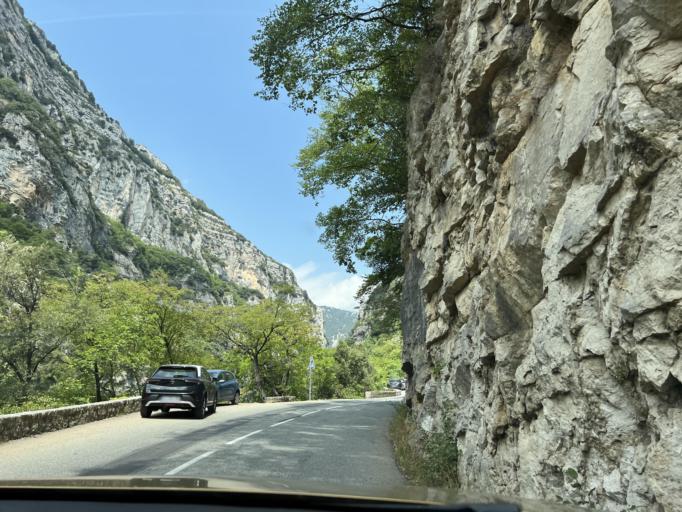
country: FR
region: Provence-Alpes-Cote d'Azur
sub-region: Departement des Alpes-Maritimes
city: Tourrettes-sur-Loup
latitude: 43.7315
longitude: 6.9985
